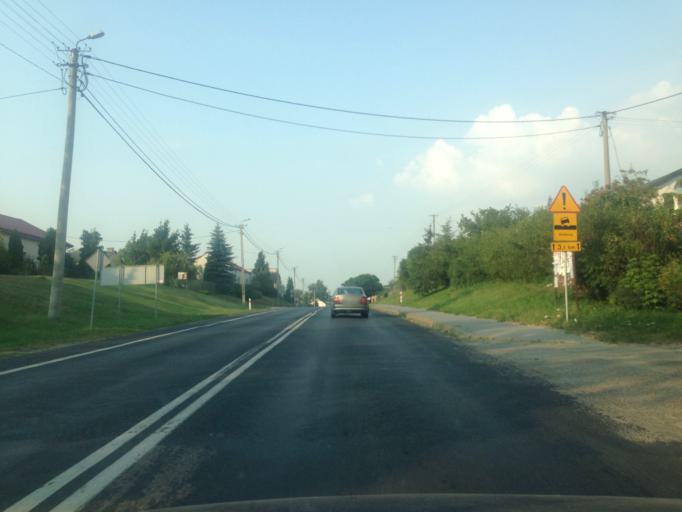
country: PL
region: Kujawsko-Pomorskie
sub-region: Powiat lipnowski
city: Lipno
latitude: 52.8088
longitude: 19.1344
